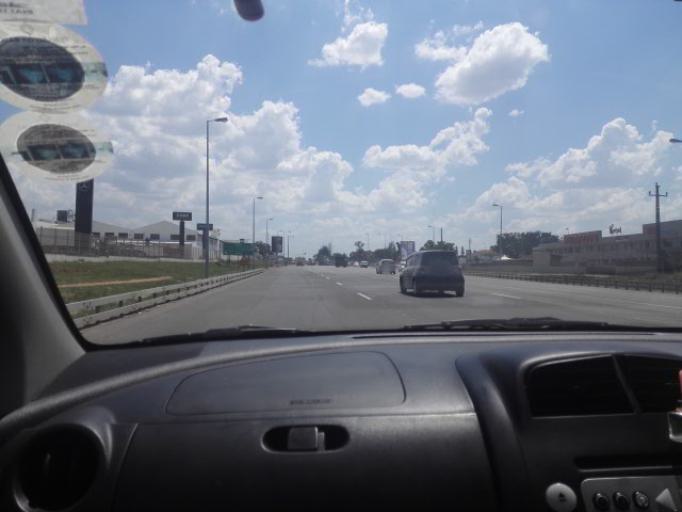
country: MZ
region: Maputo
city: Matola
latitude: -25.9529
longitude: 32.4628
